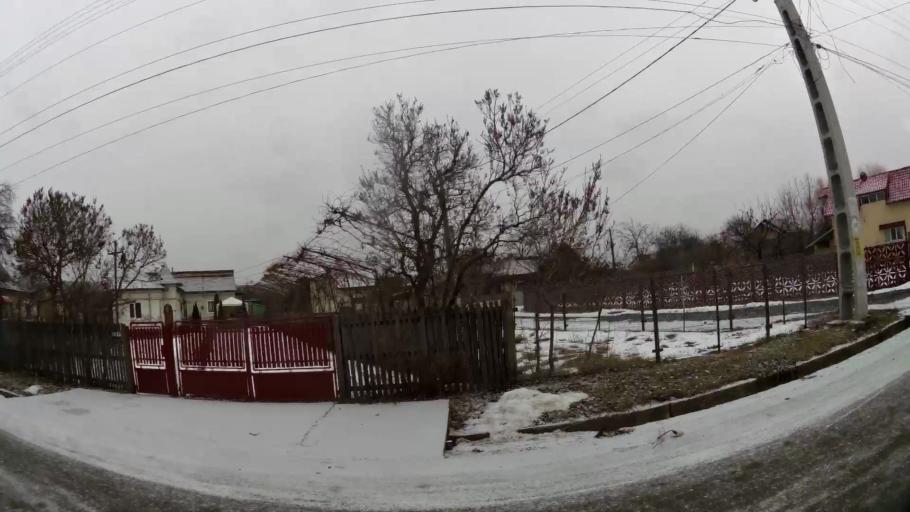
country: RO
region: Dambovita
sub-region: Municipiul Targoviste
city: Targoviste
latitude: 44.9415
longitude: 25.4751
